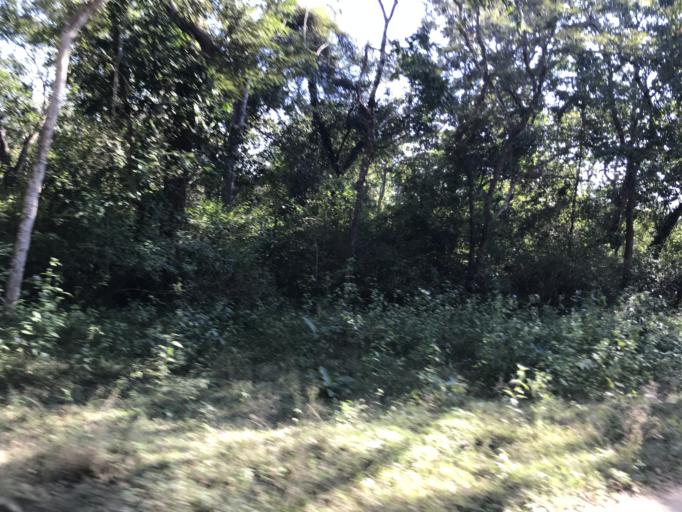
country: IN
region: Karnataka
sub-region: Mysore
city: Heggadadevankote
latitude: 11.9611
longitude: 76.2385
